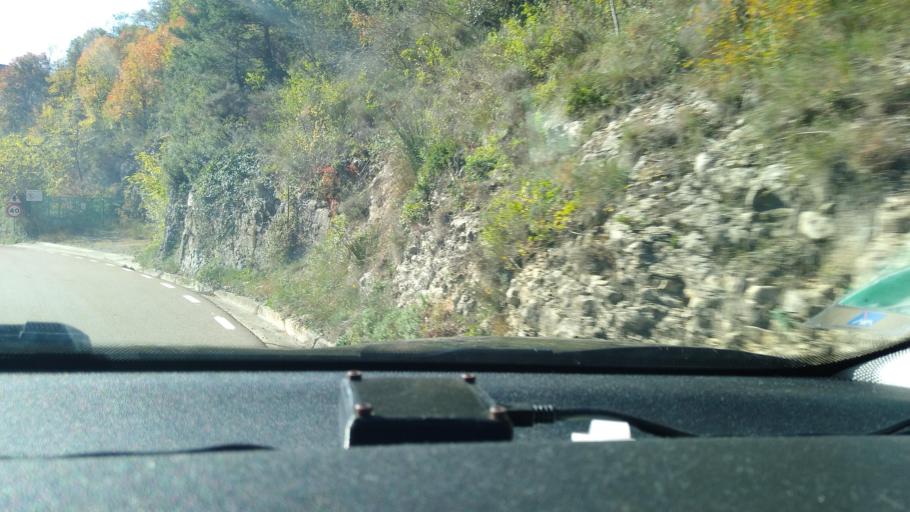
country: ES
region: Catalonia
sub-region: Provincia de Barcelona
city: Vallcebre
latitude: 42.1783
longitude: 1.8600
